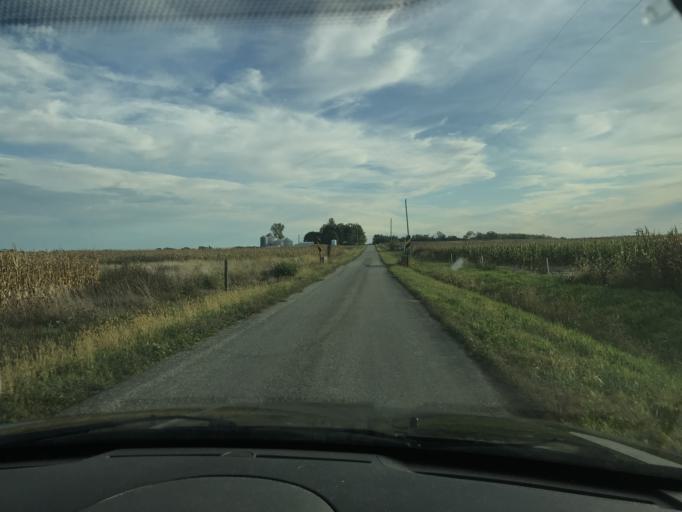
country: US
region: Ohio
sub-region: Logan County
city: West Liberty
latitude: 40.2115
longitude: -83.8083
